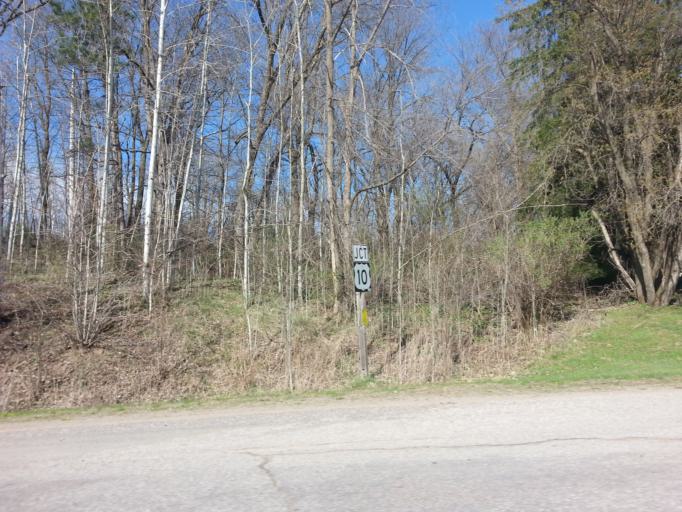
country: US
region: Wisconsin
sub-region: Pierce County
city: Ellsworth
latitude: 44.7311
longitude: -92.5785
